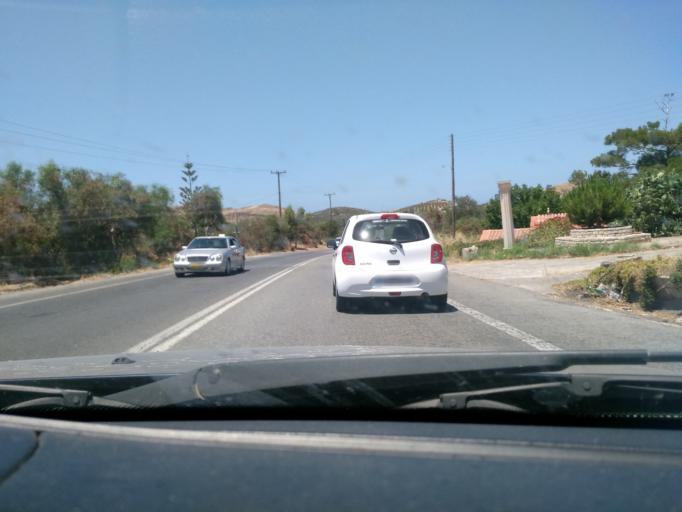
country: GR
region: Crete
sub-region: Nomos Rethymnis
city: Panormos
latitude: 35.4095
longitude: 24.7231
